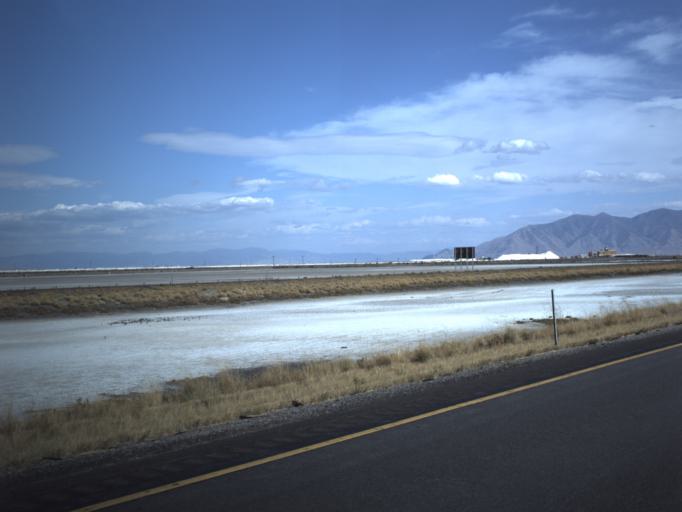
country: US
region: Utah
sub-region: Tooele County
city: Grantsville
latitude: 40.7128
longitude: -112.5381
